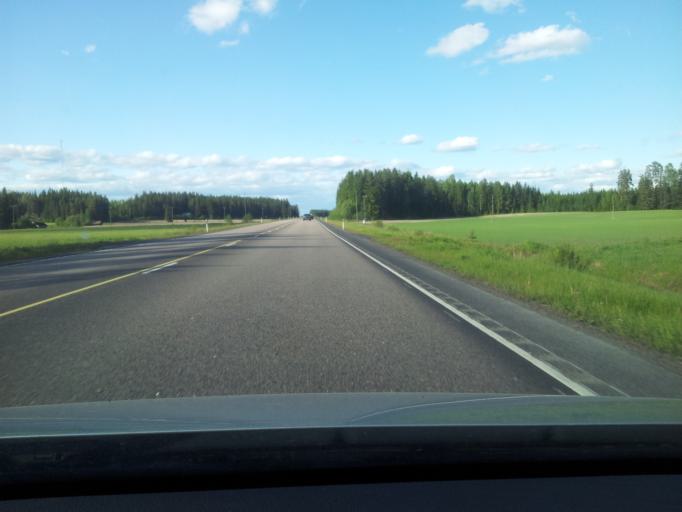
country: FI
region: Kymenlaakso
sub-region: Kouvola
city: Elimaeki
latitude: 60.7744
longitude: 26.4826
